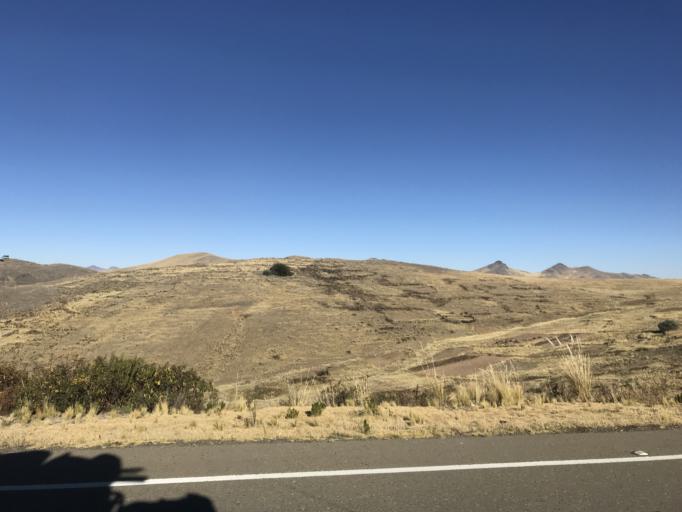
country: PE
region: Puno
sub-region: Yunguyo
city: Yunguyo
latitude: -16.1869
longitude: -68.9787
